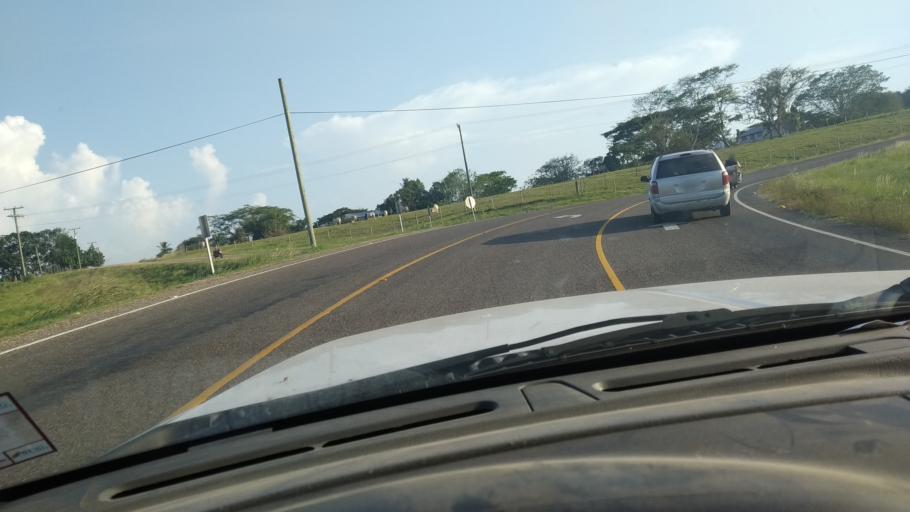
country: BZ
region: Cayo
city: San Ignacio
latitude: 17.2449
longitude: -88.9875
